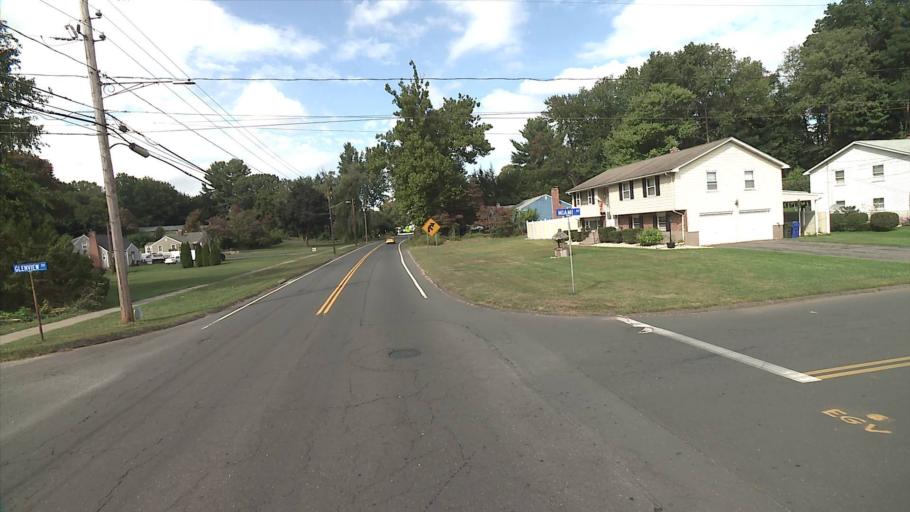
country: US
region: Connecticut
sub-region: Hartford County
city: Newington
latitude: 41.6809
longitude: -72.7220
